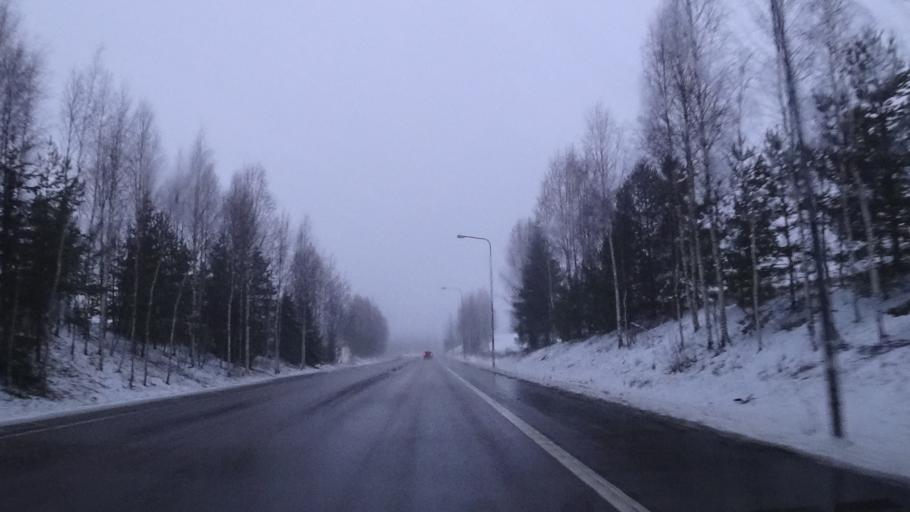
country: FI
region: Paijanne Tavastia
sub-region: Lahti
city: Hollola
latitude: 60.9825
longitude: 25.4599
